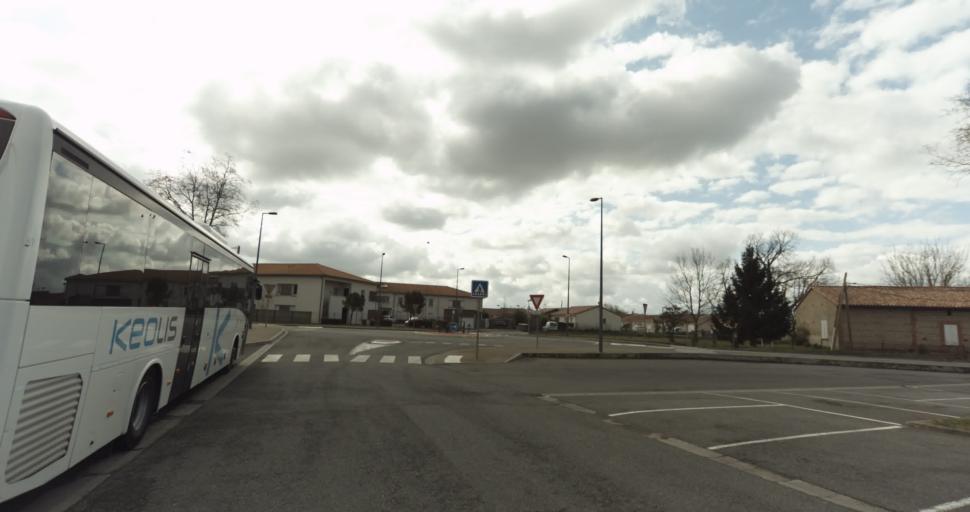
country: FR
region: Midi-Pyrenees
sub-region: Departement de la Haute-Garonne
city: Auterive
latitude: 43.3507
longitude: 1.4612
